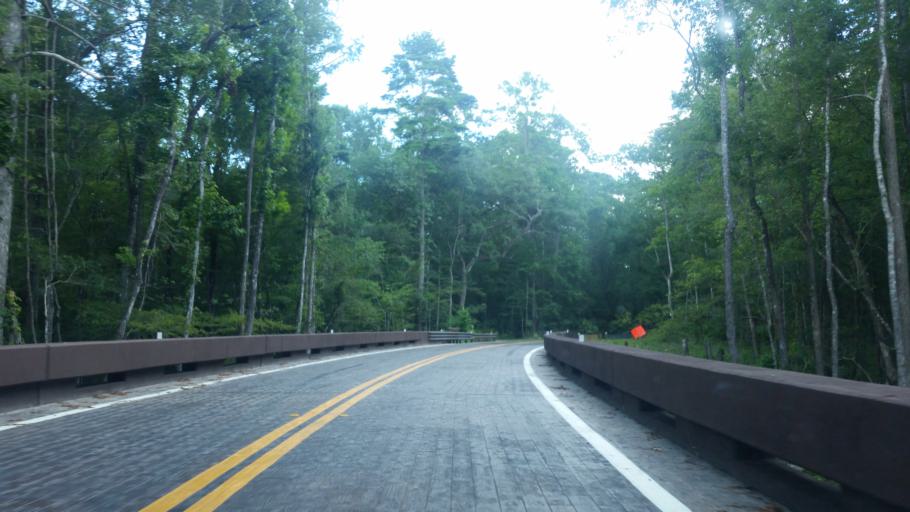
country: US
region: Florida
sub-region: Leon County
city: Woodville
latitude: 30.2854
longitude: -84.1494
